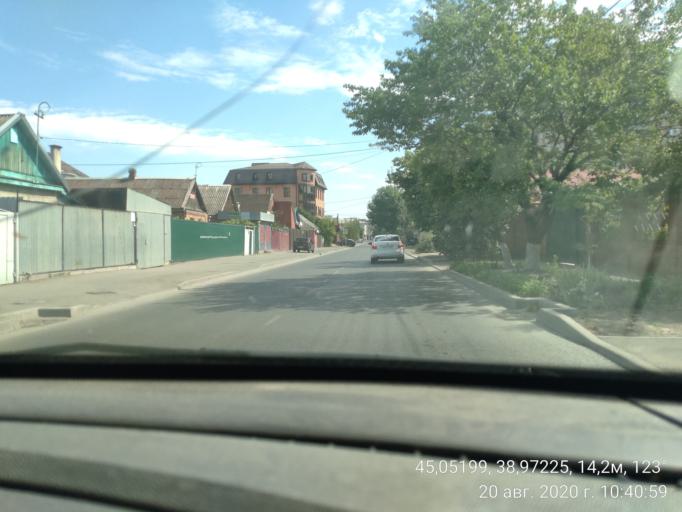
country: RU
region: Krasnodarskiy
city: Krasnodar
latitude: 45.0520
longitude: 38.9722
